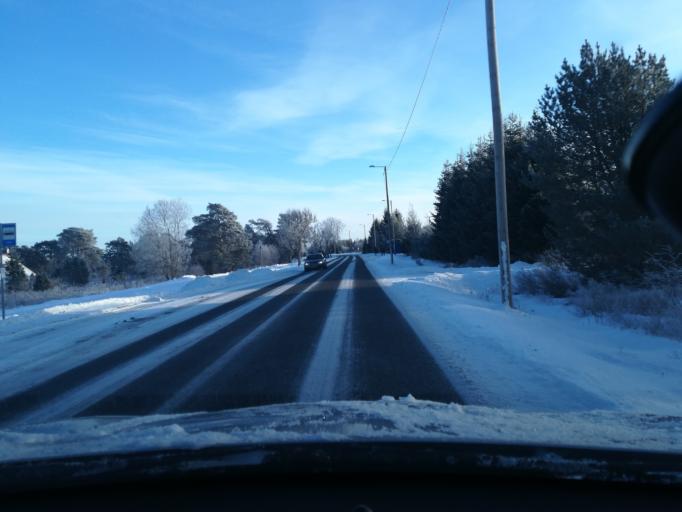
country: EE
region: Harju
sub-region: Keila linn
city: Keila
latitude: 59.3963
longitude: 24.3165
